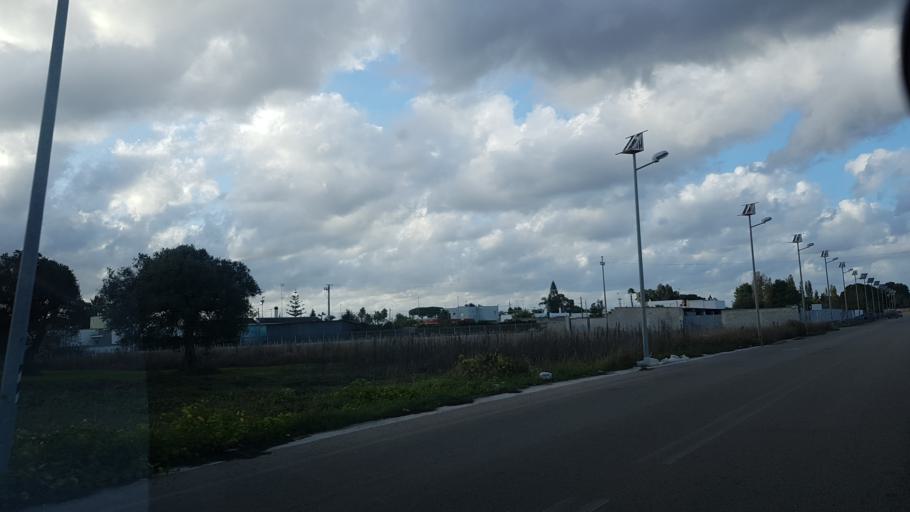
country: IT
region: Apulia
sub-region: Provincia di Brindisi
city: San Pietro Vernotico
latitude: 40.4954
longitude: 18.0076
